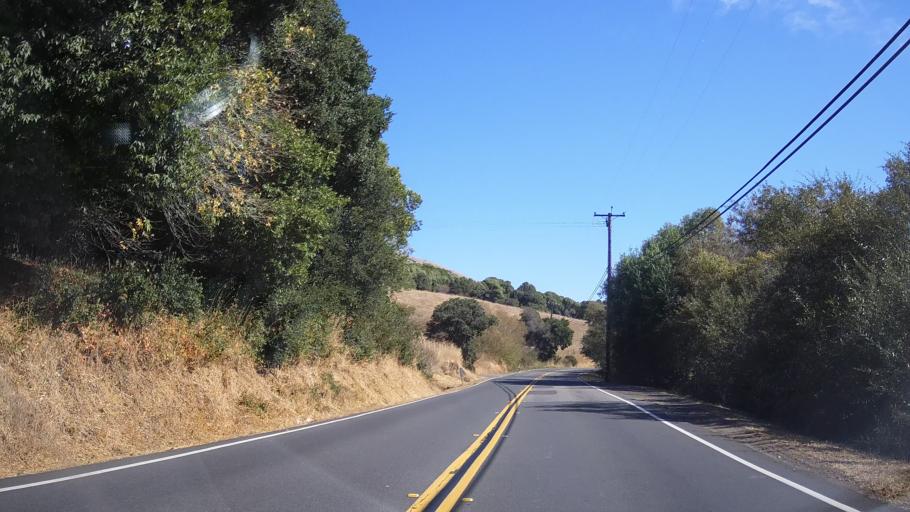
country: US
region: California
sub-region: Marin County
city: Inverness
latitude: 38.0815
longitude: -122.7797
